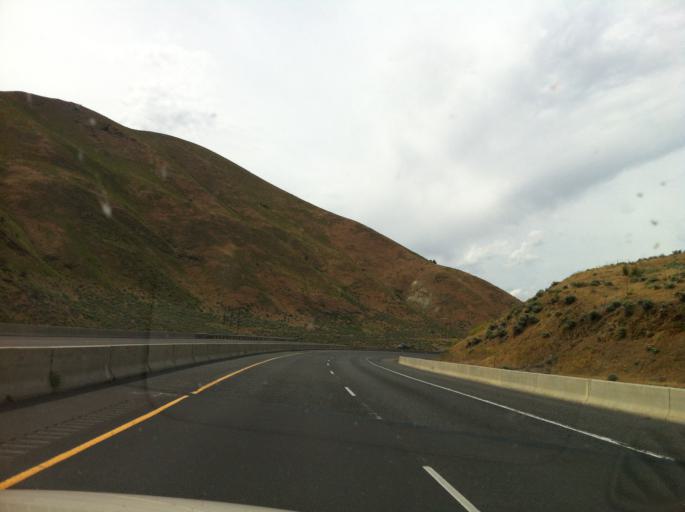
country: US
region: Idaho
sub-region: Washington County
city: Weiser
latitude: 44.4162
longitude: -117.3083
